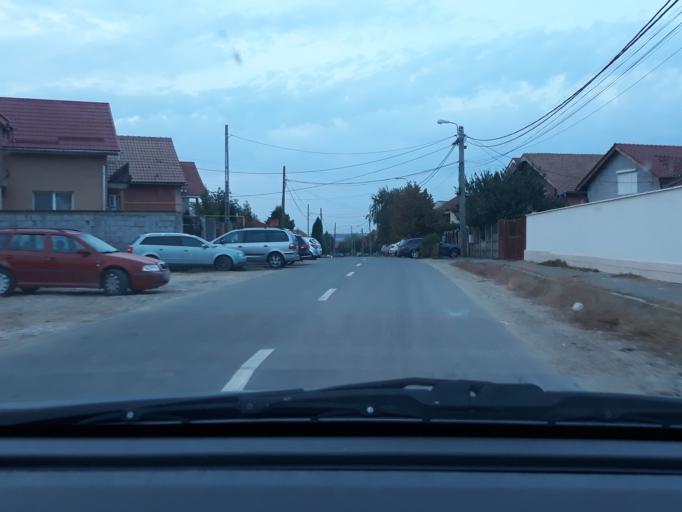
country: RO
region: Bihor
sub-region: Comuna Biharea
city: Oradea
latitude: 47.0269
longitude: 21.9356
